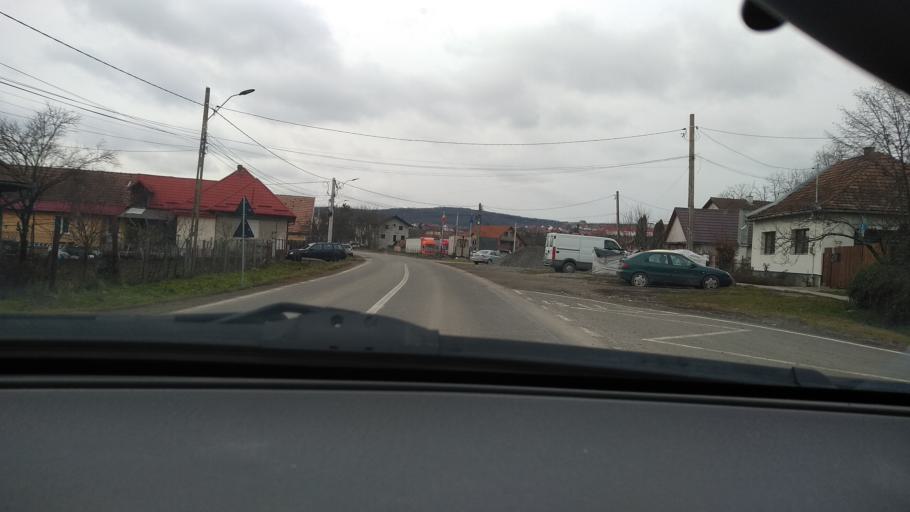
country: RO
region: Mures
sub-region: Comuna Livezeni
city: Livezeni
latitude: 46.5469
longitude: 24.6376
